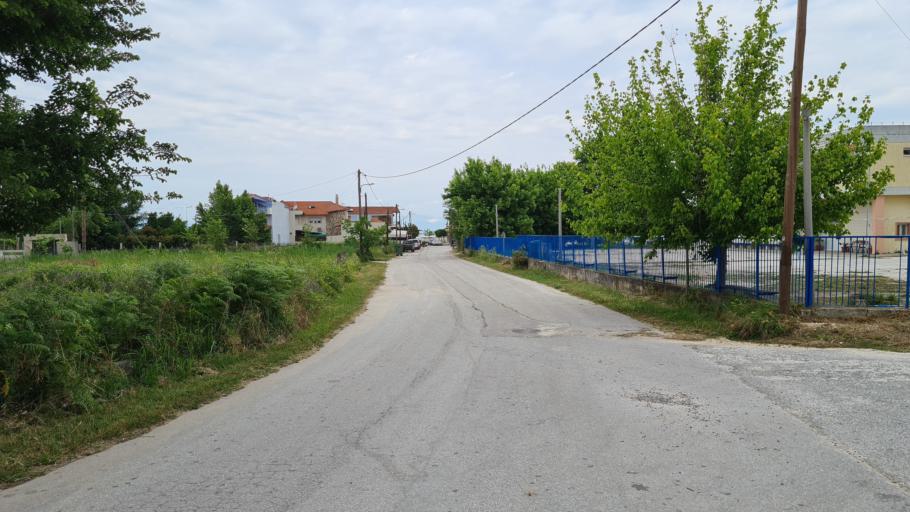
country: GR
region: East Macedonia and Thrace
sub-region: Nomos Kavalas
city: Thasos
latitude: 40.7763
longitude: 24.7016
